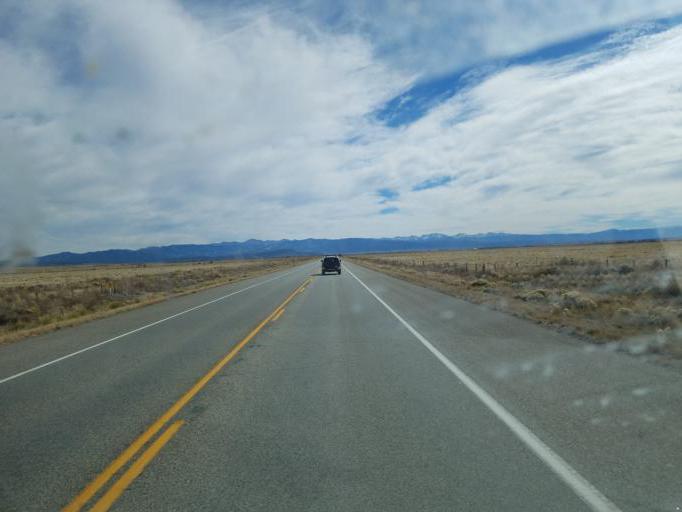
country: US
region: Colorado
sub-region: Alamosa County
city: Alamosa East
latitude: 37.4636
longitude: -105.5649
